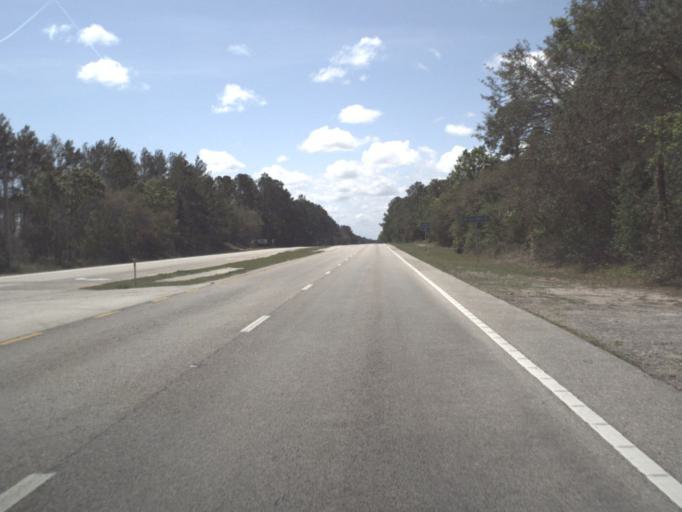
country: US
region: Florida
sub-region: Flagler County
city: Palm Coast
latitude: 29.6429
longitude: -81.2859
